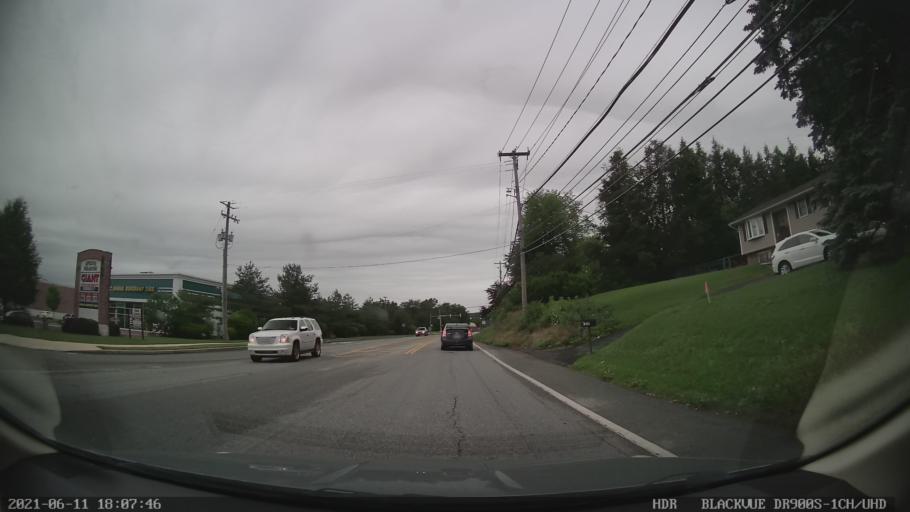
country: US
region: Pennsylvania
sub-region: Berks County
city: Whitfield
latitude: 40.3451
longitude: -76.0008
